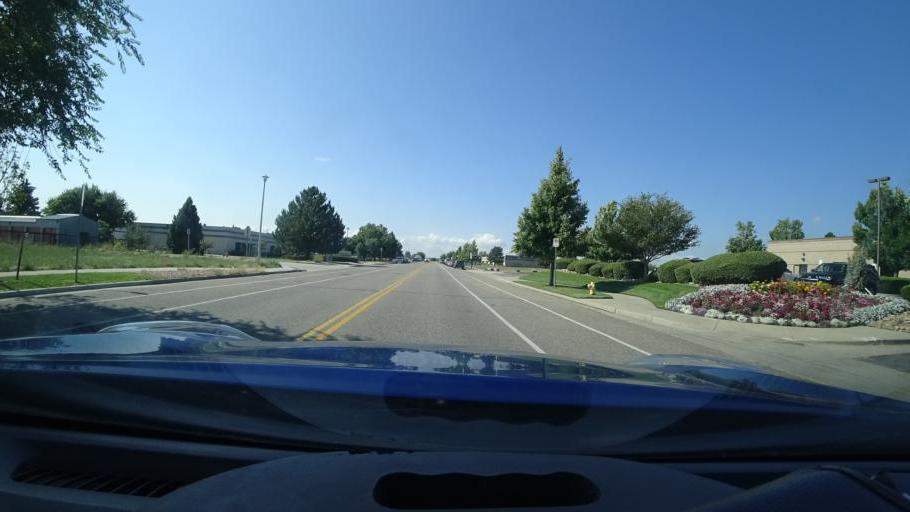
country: US
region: Colorado
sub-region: Adams County
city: Aurora
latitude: 39.7244
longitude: -104.8006
